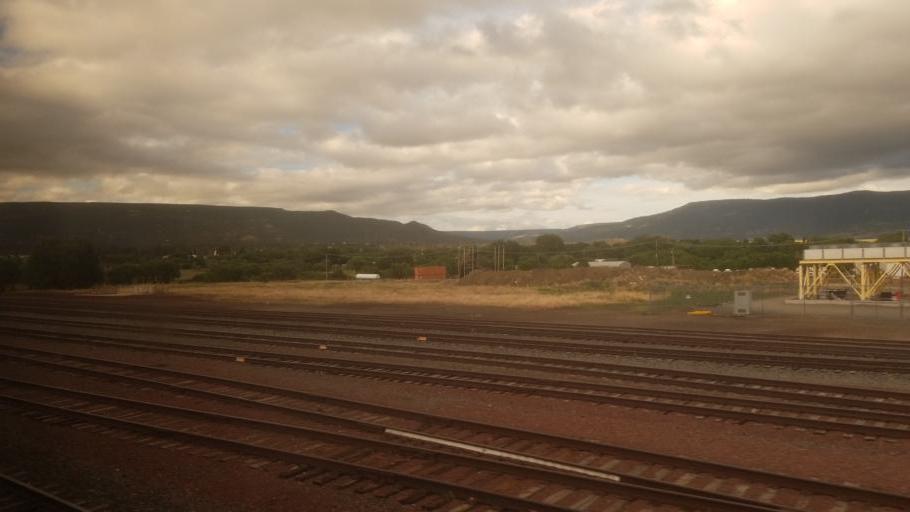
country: US
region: New Mexico
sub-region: Colfax County
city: Raton
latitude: 36.8942
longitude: -104.4390
